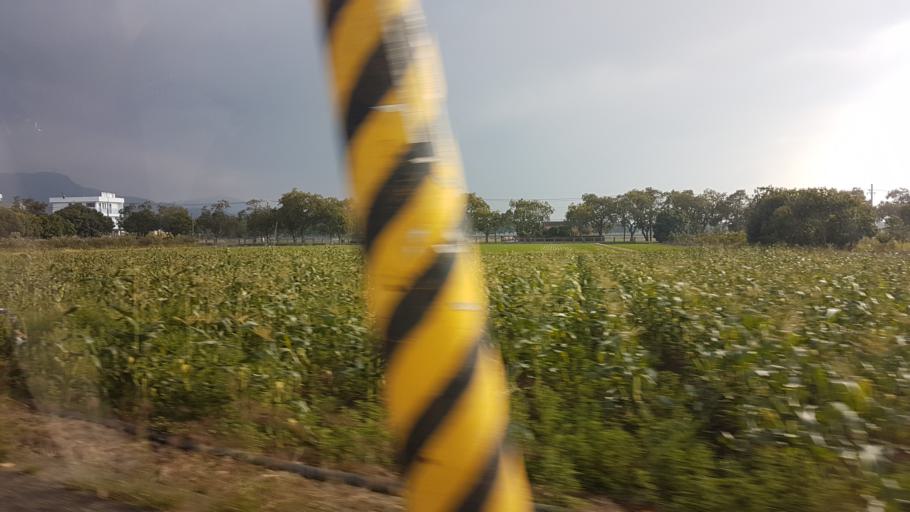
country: TW
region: Taiwan
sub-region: Chiayi
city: Jiayi Shi
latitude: 23.3778
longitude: 120.4412
